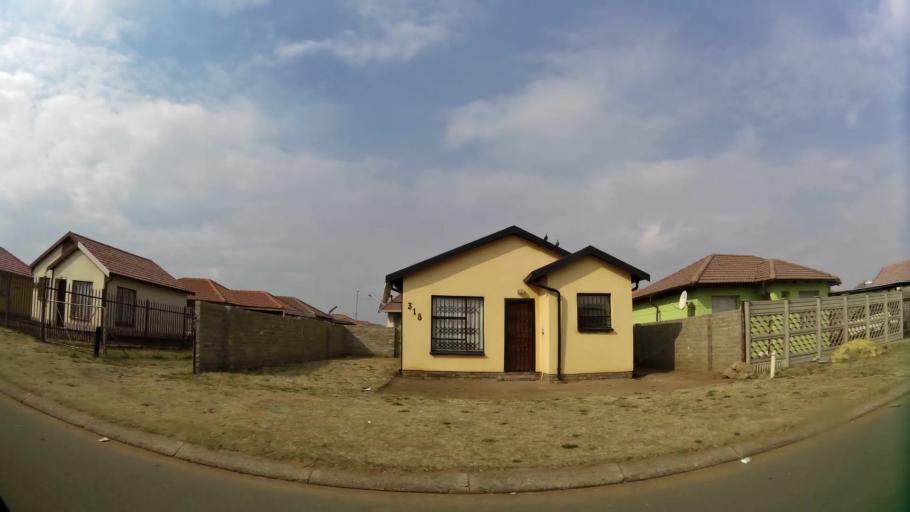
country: ZA
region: Gauteng
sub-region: Sedibeng District Municipality
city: Vanderbijlpark
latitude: -26.6837
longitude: 27.8425
